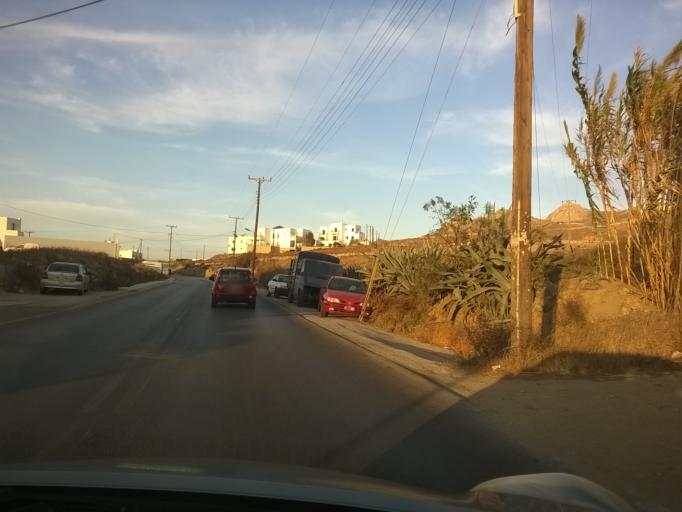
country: GR
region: South Aegean
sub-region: Nomos Kykladon
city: Naxos
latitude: 37.1079
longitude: 25.3832
